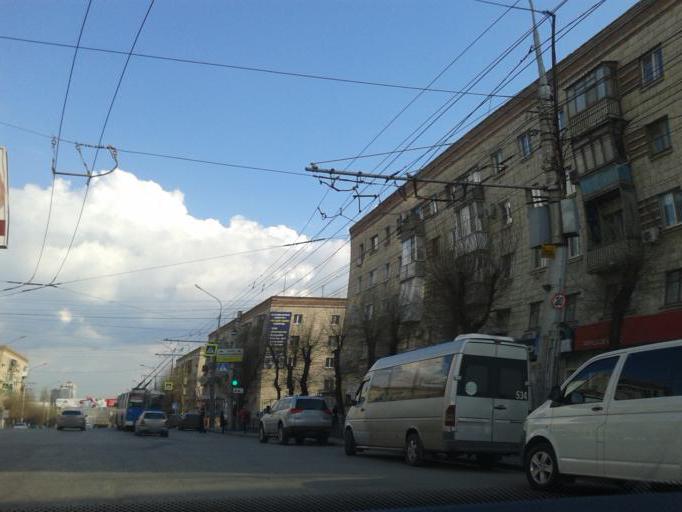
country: RU
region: Volgograd
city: Volgograd
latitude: 48.7165
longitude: 44.5100
